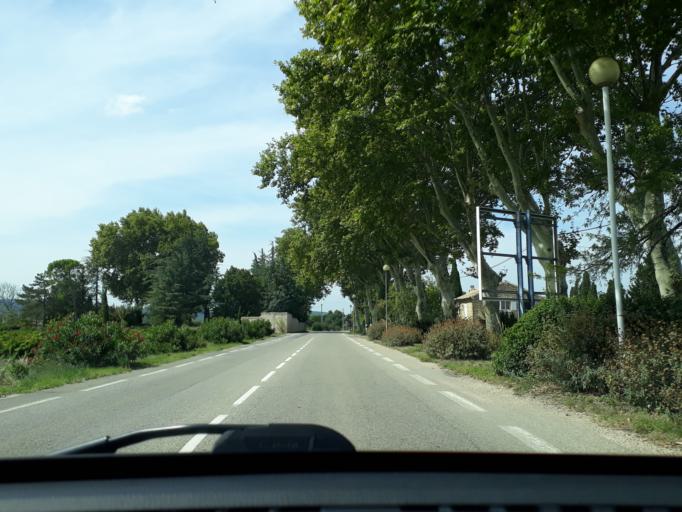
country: FR
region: Provence-Alpes-Cote d'Azur
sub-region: Departement du Vaucluse
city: Sainte-Cecile-les-Vignes
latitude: 44.2476
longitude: 4.8778
